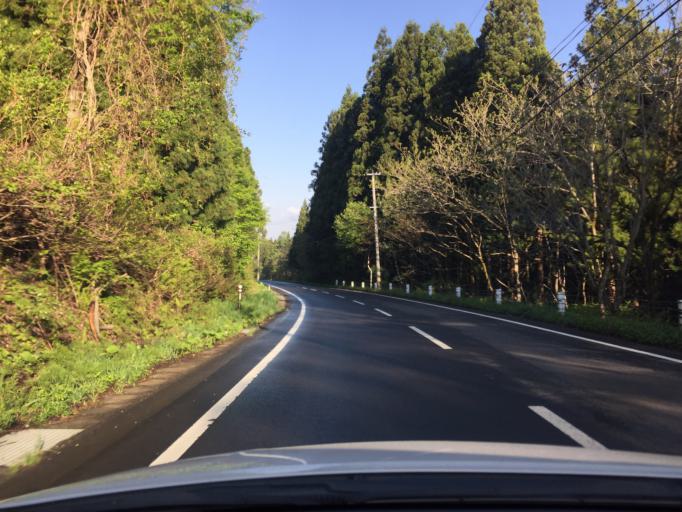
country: JP
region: Fukushima
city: Kitakata
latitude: 37.6616
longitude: 139.9983
